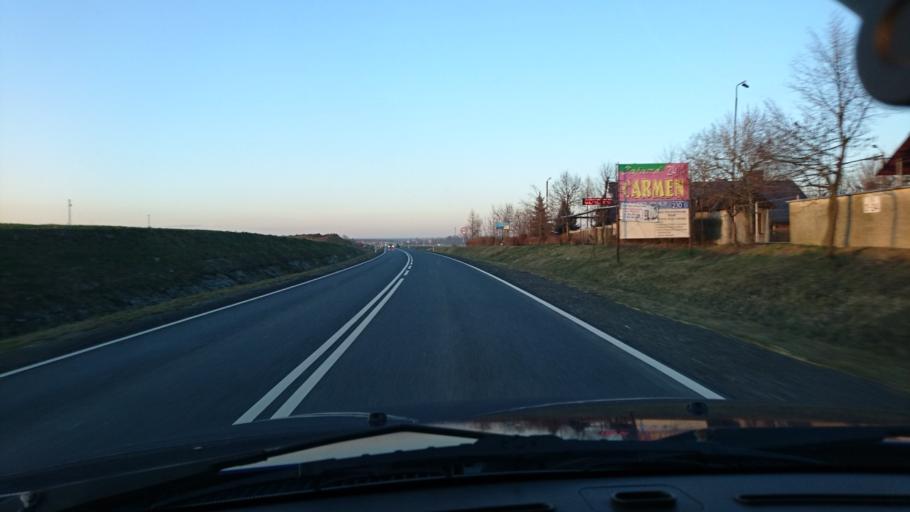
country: PL
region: Silesian Voivodeship
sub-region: Powiat gliwicki
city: Wielowies
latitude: 50.4942
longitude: 18.6074
